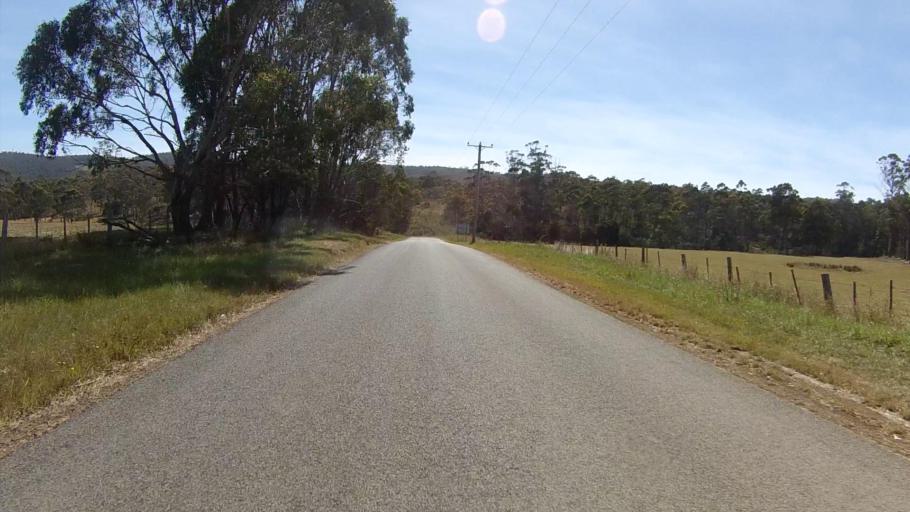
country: AU
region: Tasmania
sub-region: Sorell
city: Sorell
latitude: -42.7491
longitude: 147.7182
